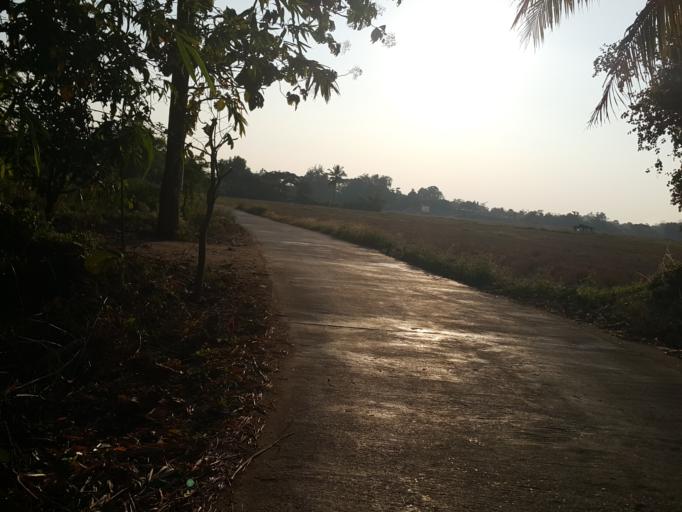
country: TH
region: Chiang Mai
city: Mae On
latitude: 18.7571
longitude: 99.2567
